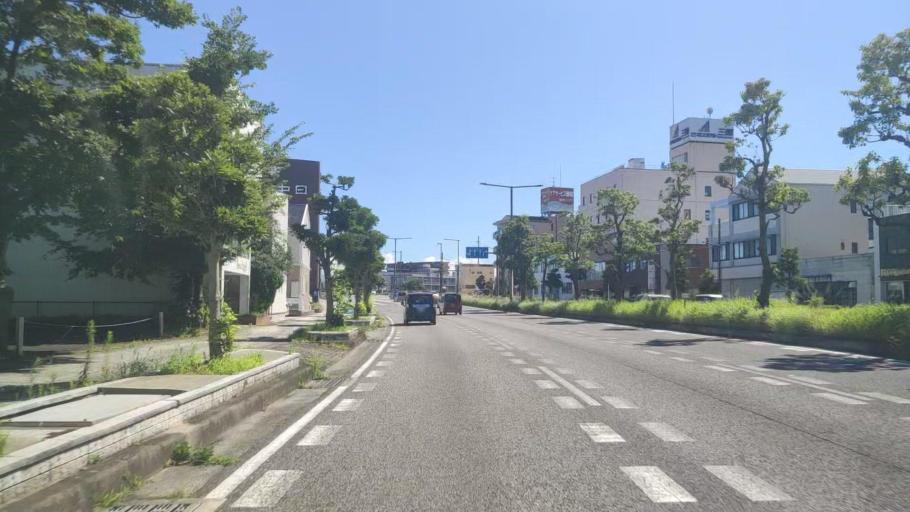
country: JP
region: Mie
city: Tsu-shi
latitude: 34.7274
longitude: 136.5114
